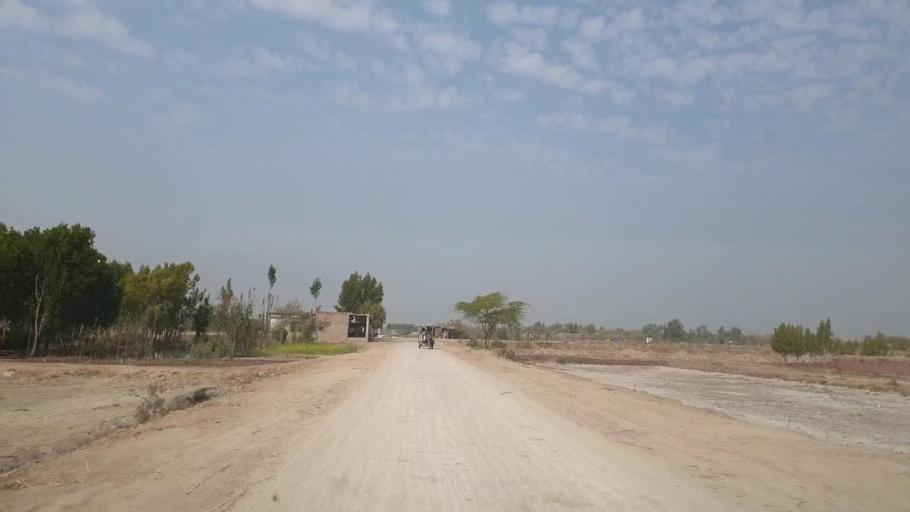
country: PK
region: Sindh
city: Mirpur Khas
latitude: 25.5505
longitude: 69.0791
